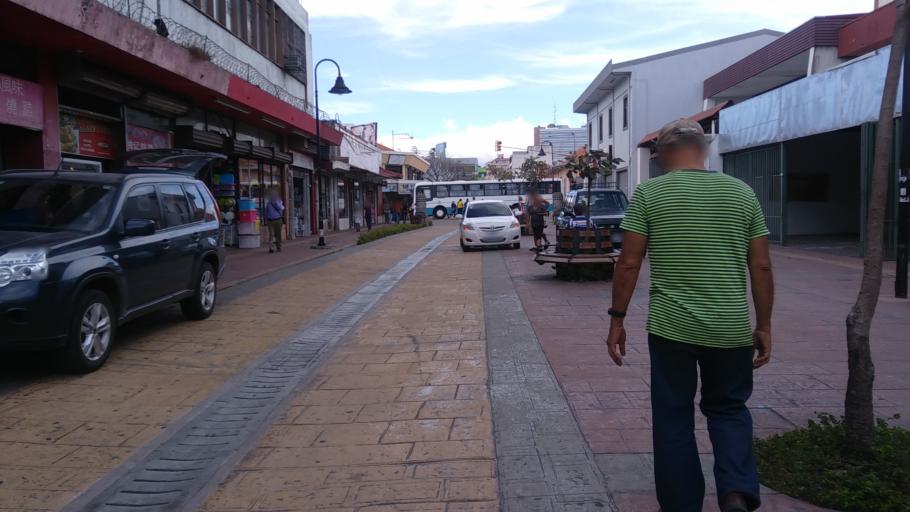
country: CR
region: San Jose
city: San Jose
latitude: 9.9307
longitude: -84.0751
